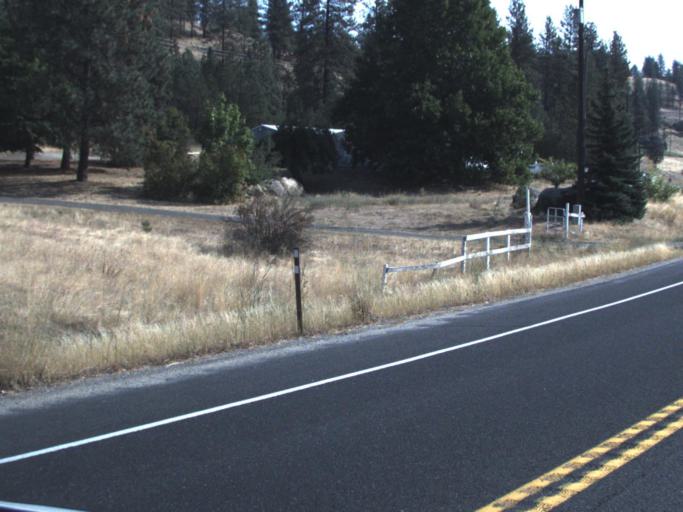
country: US
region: Washington
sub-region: Spokane County
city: Town and Country
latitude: 47.7586
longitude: -117.5298
